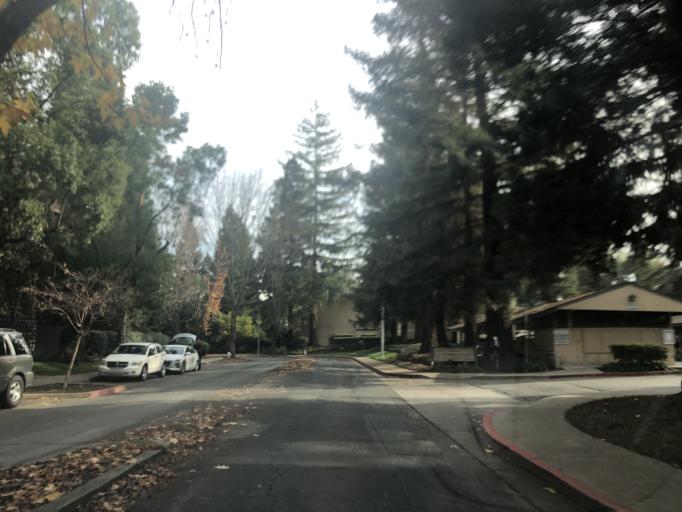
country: US
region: California
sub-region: Contra Costa County
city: Concord
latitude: 37.9990
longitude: -122.0410
